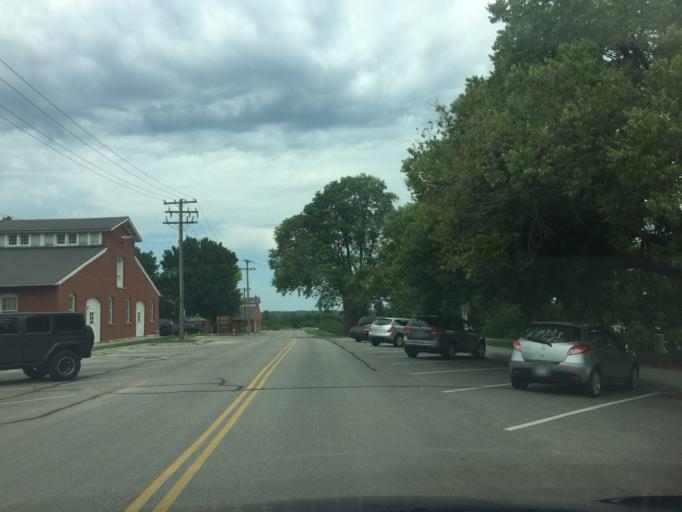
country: US
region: Kansas
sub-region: Leavenworth County
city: Leavenworth
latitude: 39.3597
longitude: -94.9191
